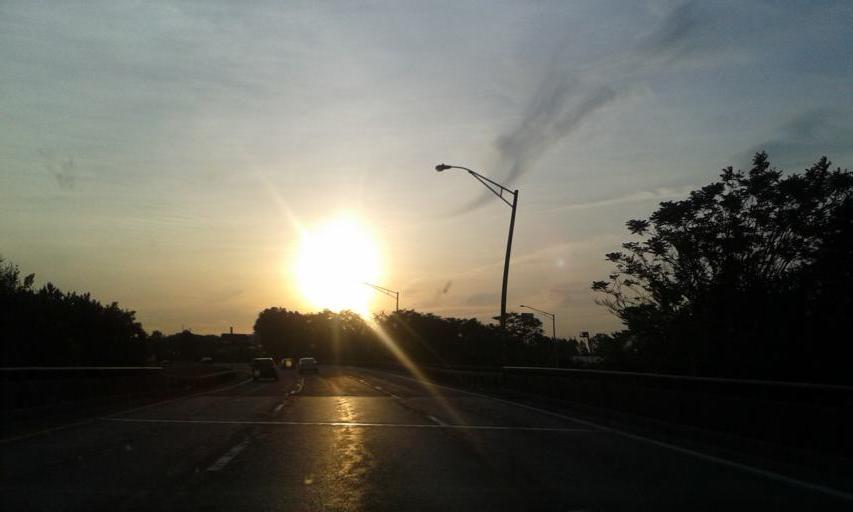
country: US
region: New York
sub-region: Onondaga County
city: Syracuse
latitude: 43.0565
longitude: -76.1754
